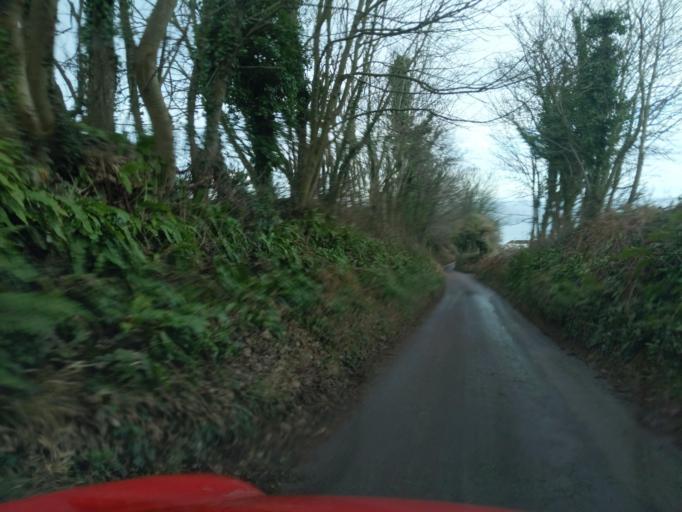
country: GB
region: England
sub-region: Devon
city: Salcombe
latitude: 50.2526
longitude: -3.6643
